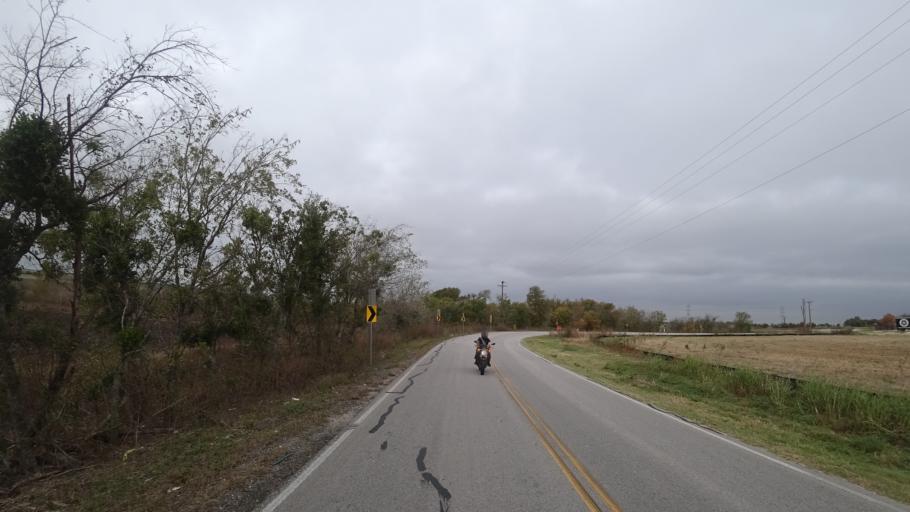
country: US
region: Texas
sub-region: Travis County
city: Manor
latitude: 30.4077
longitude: -97.5605
